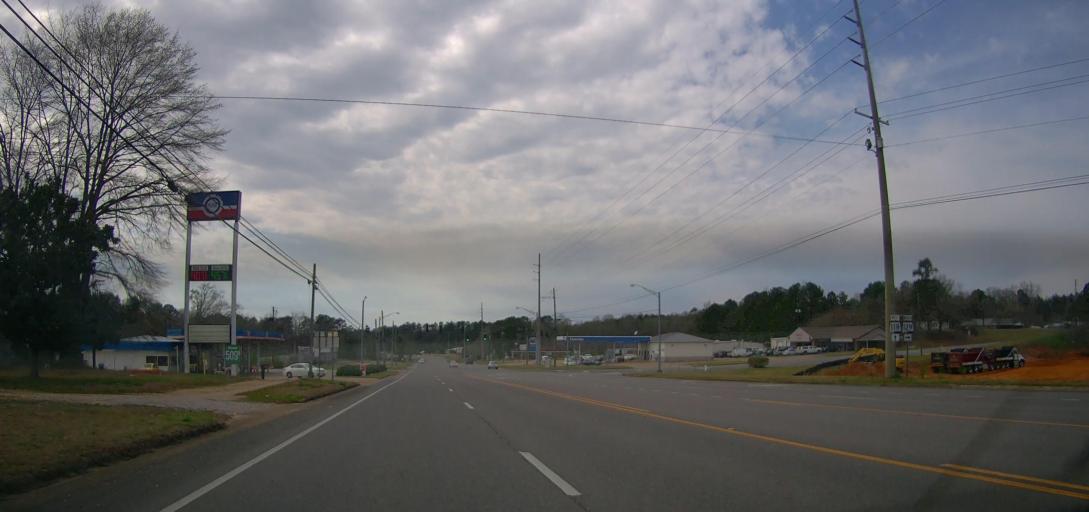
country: US
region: Alabama
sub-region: Marion County
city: Winfield
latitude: 33.9316
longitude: -87.7821
